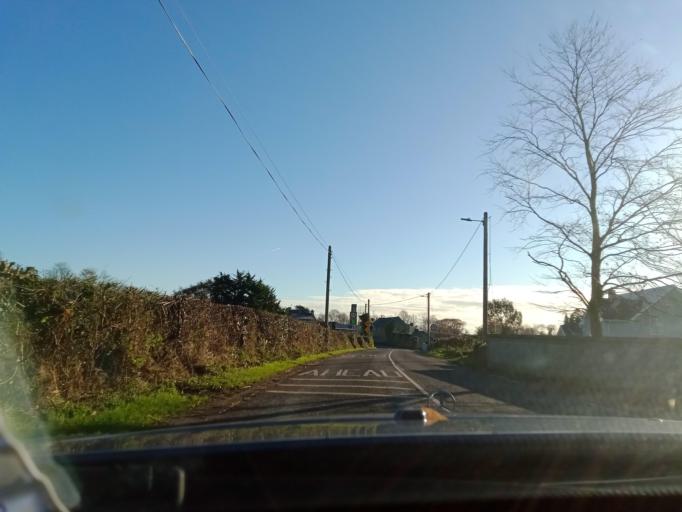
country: IE
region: Leinster
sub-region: Kilkenny
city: Piltown
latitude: 52.3886
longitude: -7.3462
